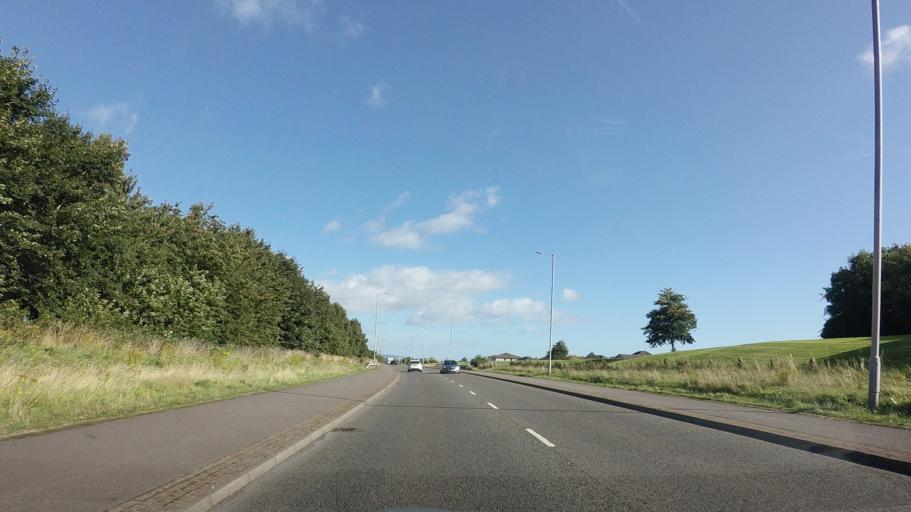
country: GB
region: Scotland
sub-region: Highland
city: Inverness
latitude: 57.4612
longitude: -4.1980
